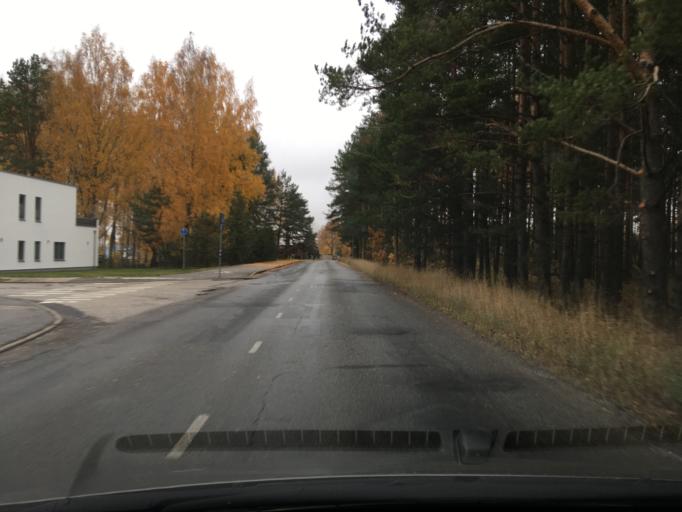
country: EE
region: Tartu
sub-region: Tartu linn
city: Tartu
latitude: 58.3504
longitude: 26.7678
